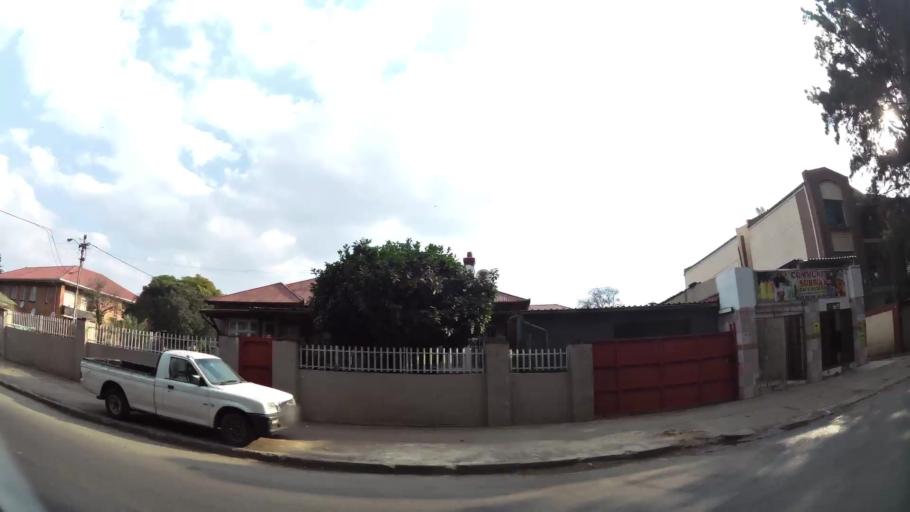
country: ZA
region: Gauteng
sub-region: Ekurhuleni Metropolitan Municipality
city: Germiston
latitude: -26.2232
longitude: 28.1694
